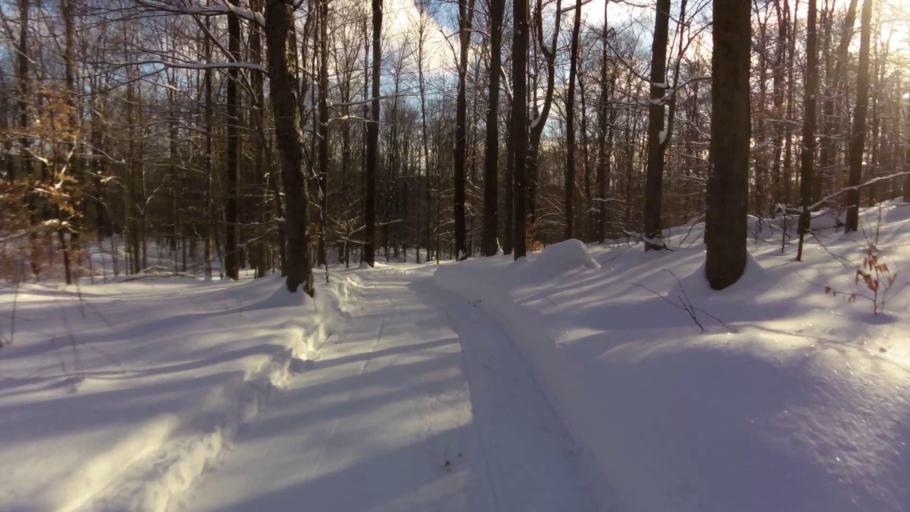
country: US
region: New York
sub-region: Chautauqua County
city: Falconer
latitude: 42.2578
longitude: -79.1615
